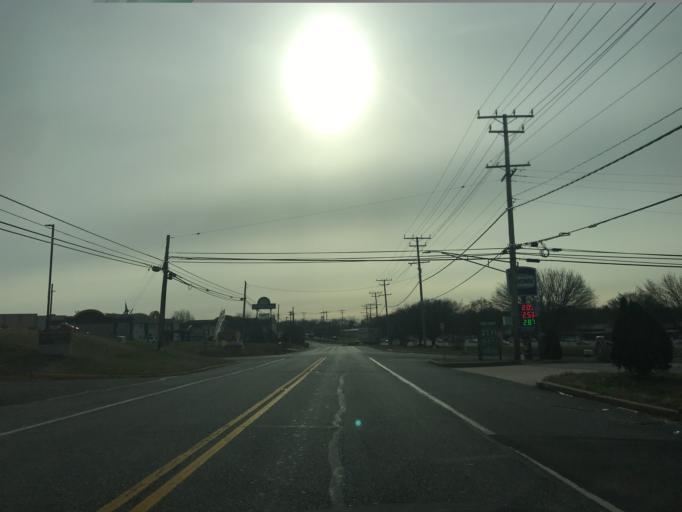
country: US
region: Maryland
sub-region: Harford County
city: Aberdeen
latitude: 39.5230
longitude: -76.1888
